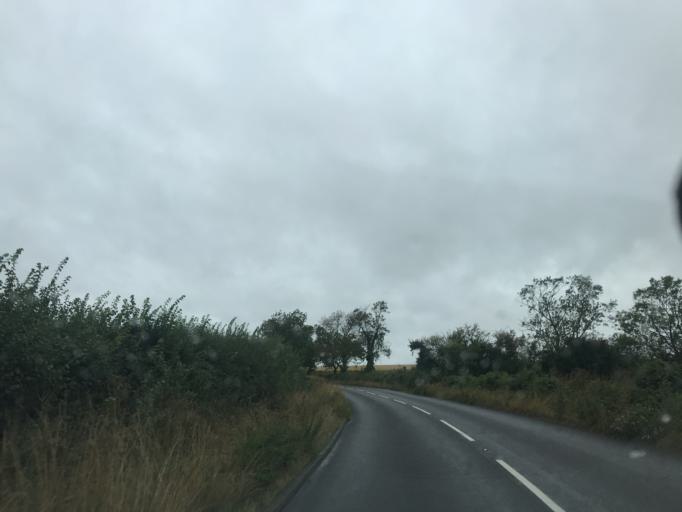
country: GB
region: England
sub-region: Buckinghamshire
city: Stone
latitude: 51.7858
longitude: -0.8738
